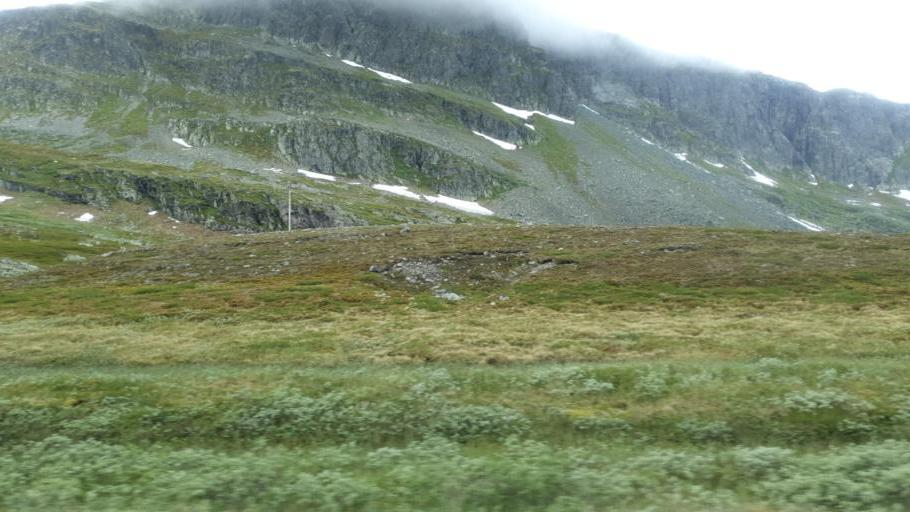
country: NO
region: Oppland
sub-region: Vestre Slidre
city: Slidre
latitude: 61.2955
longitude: 8.8141
